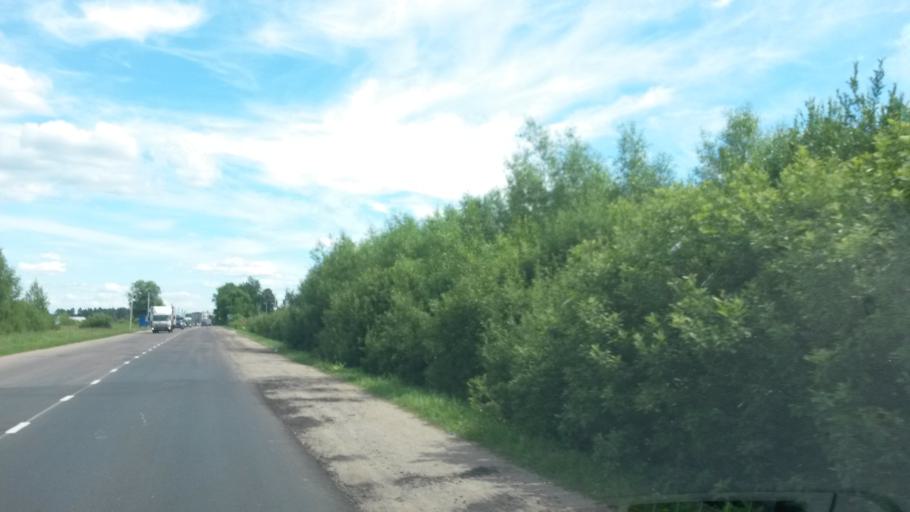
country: RU
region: Ivanovo
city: Zavolzhsk
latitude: 57.4999
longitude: 42.1205
